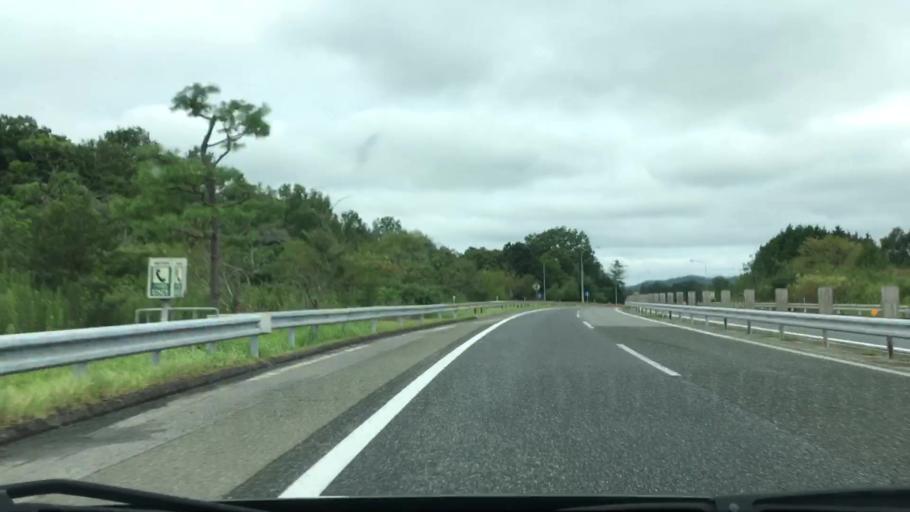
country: JP
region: Hiroshima
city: Shobara
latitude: 34.8267
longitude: 132.9586
